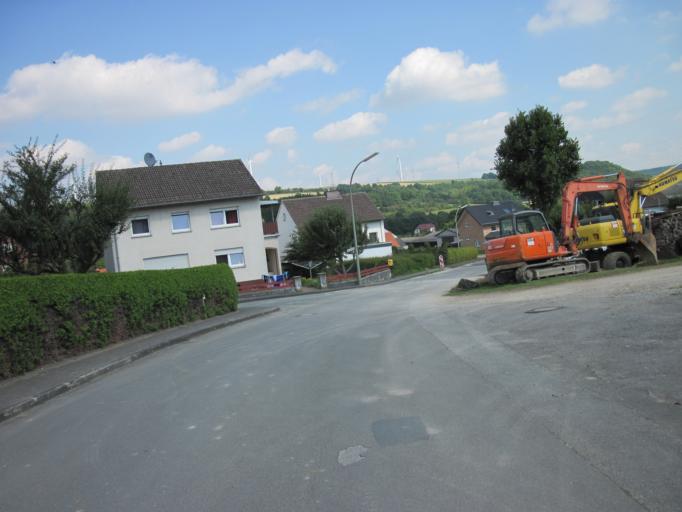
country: DE
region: North Rhine-Westphalia
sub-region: Regierungsbezirk Detmold
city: Wunnenberg
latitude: 51.5946
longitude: 8.7798
